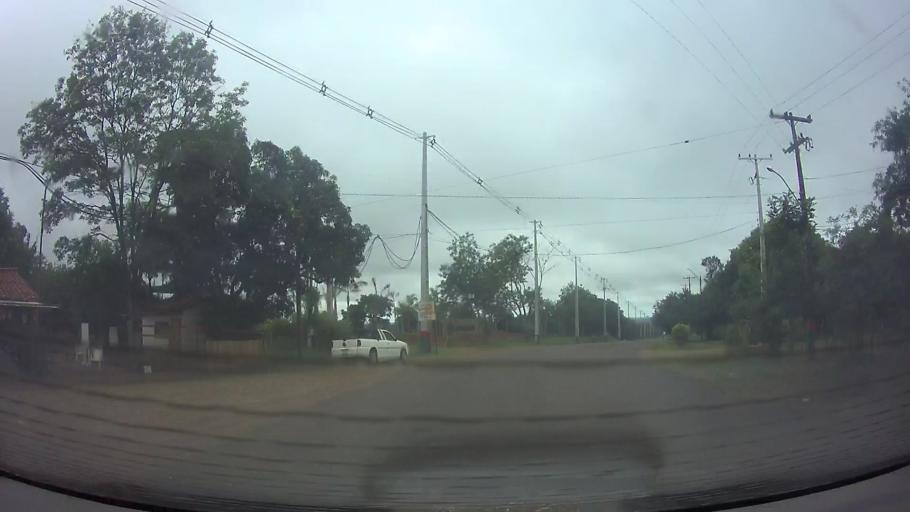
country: PY
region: Cordillera
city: Altos
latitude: -25.2739
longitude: -57.2601
